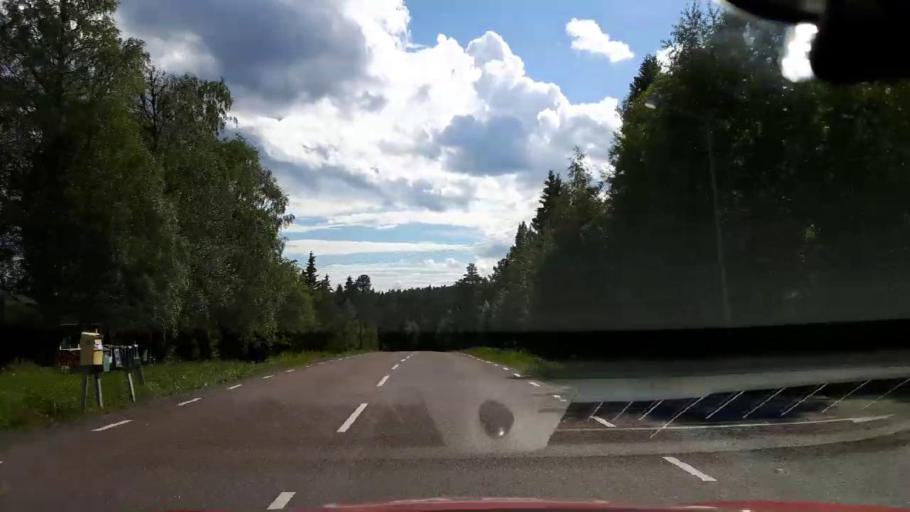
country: SE
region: Jaemtland
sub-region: Krokoms Kommun
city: Valla
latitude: 63.9857
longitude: 14.2248
